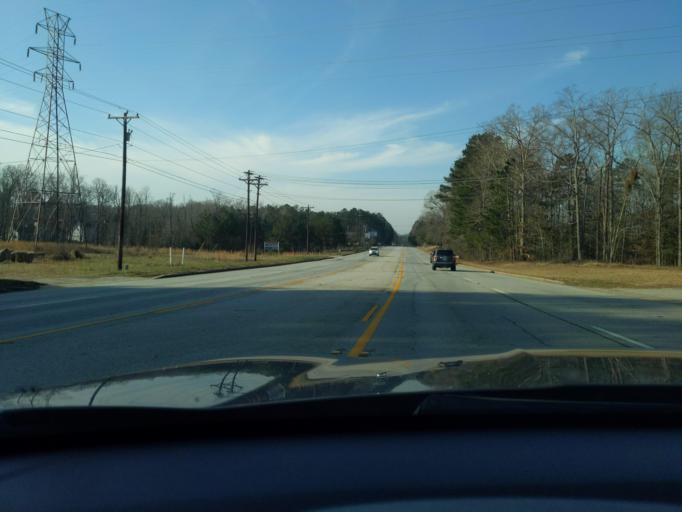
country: US
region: South Carolina
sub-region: Greenwood County
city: Greenwood
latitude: 34.2008
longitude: -82.2031
